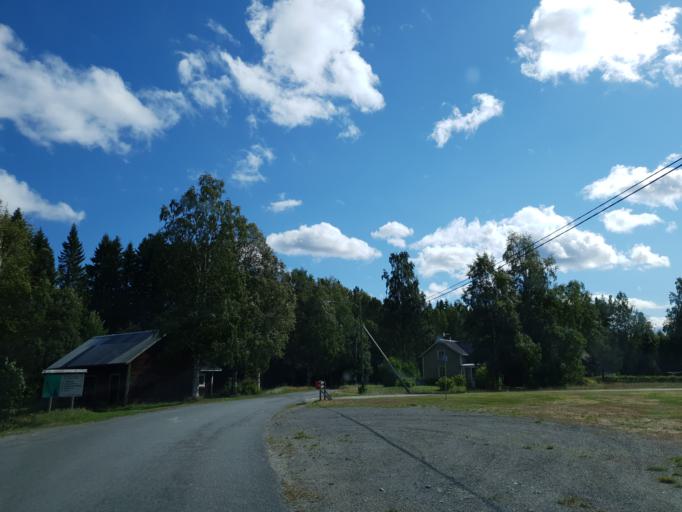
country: SE
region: Vaesternorrland
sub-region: OErnskoeldsviks Kommun
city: Husum
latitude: 63.3400
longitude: 19.1159
